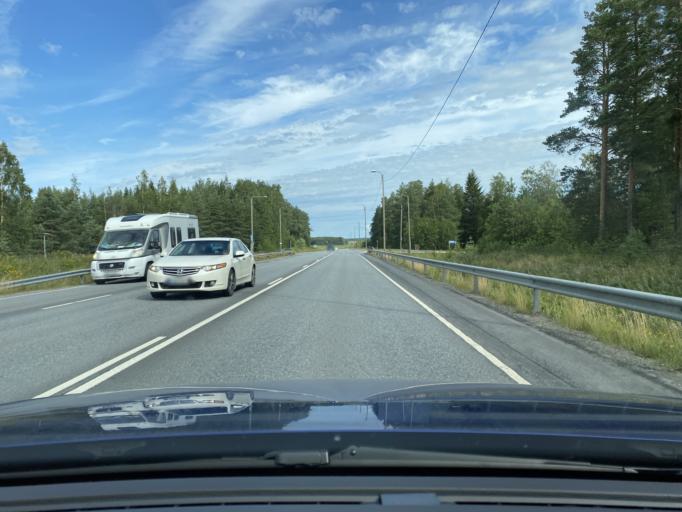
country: FI
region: Southern Ostrobothnia
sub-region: Seinaejoki
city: Ylihaermae
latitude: 63.1669
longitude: 22.8069
